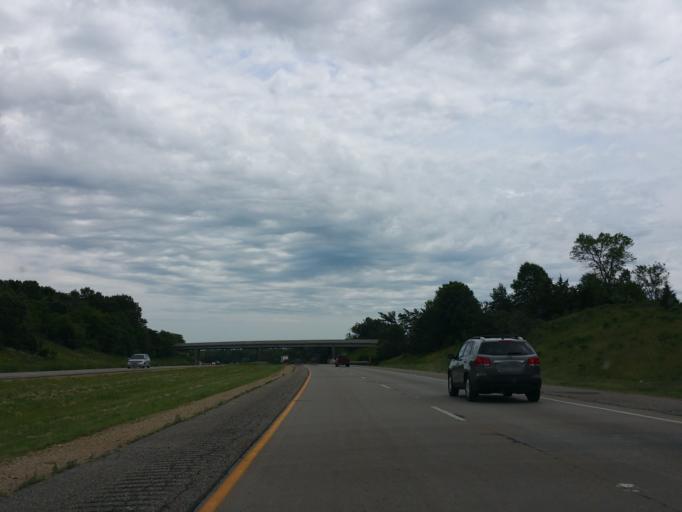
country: US
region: Wisconsin
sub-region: Juneau County
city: Mauston
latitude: 43.7858
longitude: -90.0464
